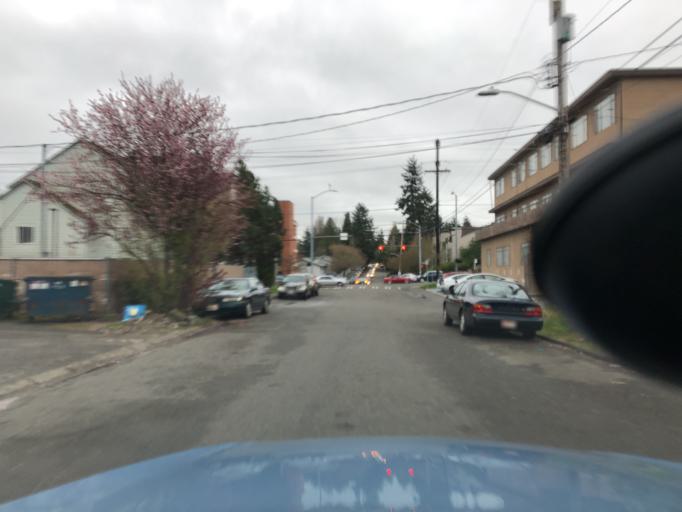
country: US
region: Washington
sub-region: King County
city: Lake Forest Park
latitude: 47.7346
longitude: -122.2965
